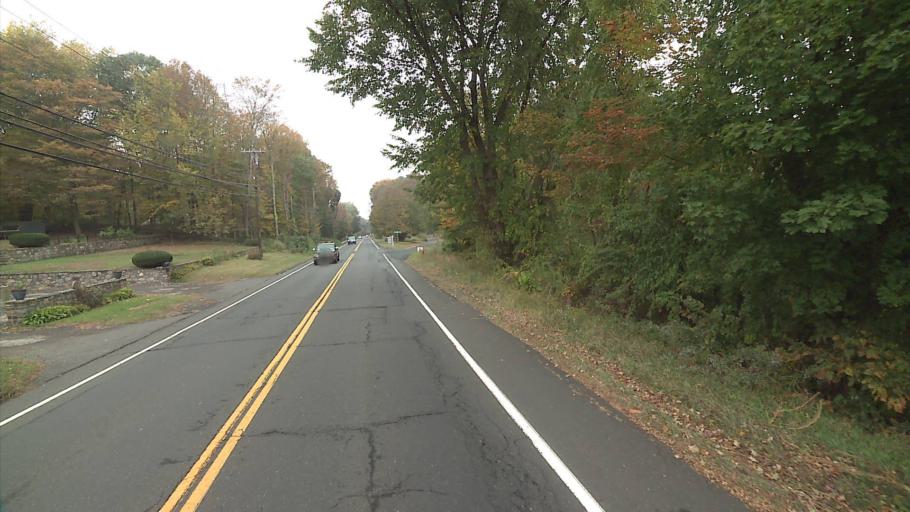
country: US
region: Connecticut
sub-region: Fairfield County
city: Newtown
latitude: 41.4193
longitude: -73.3402
